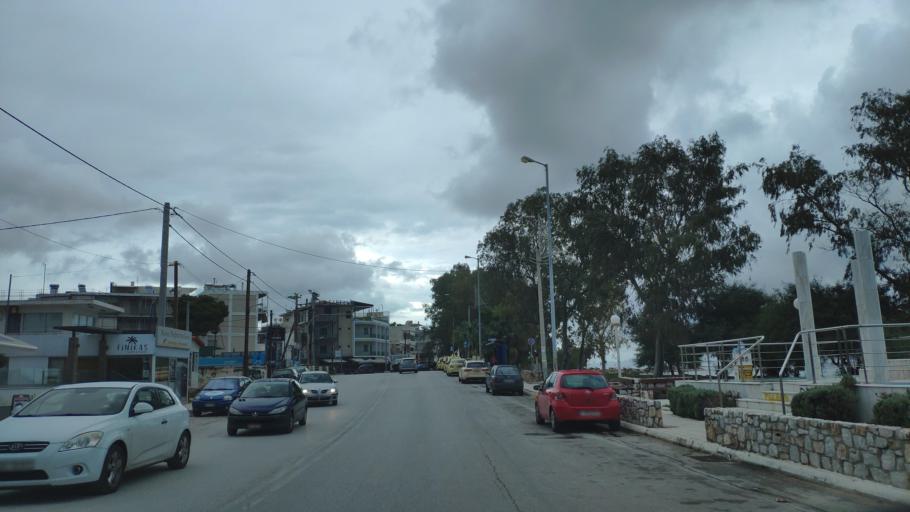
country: GR
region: Attica
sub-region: Nomarchia Anatolikis Attikis
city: Artemida
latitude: 37.9705
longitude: 24.0080
